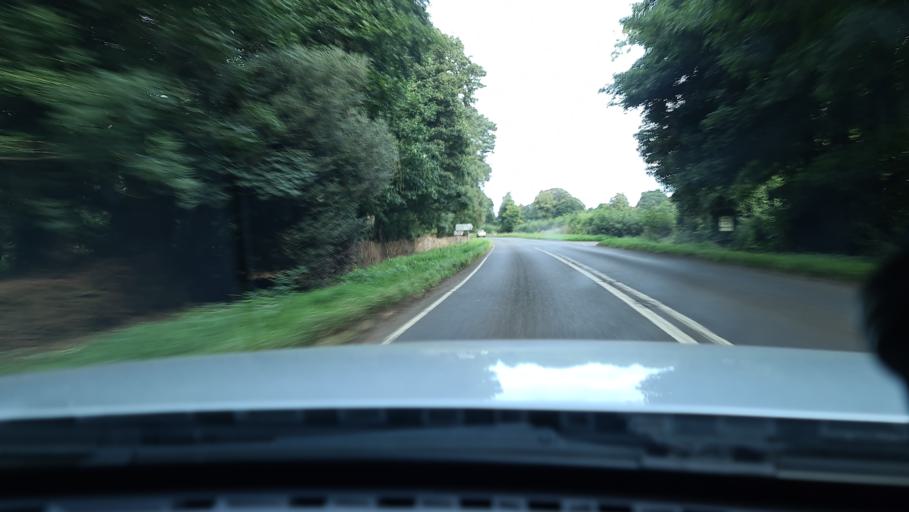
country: GB
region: England
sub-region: Oxfordshire
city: Hanwell
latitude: 52.1077
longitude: -1.4538
